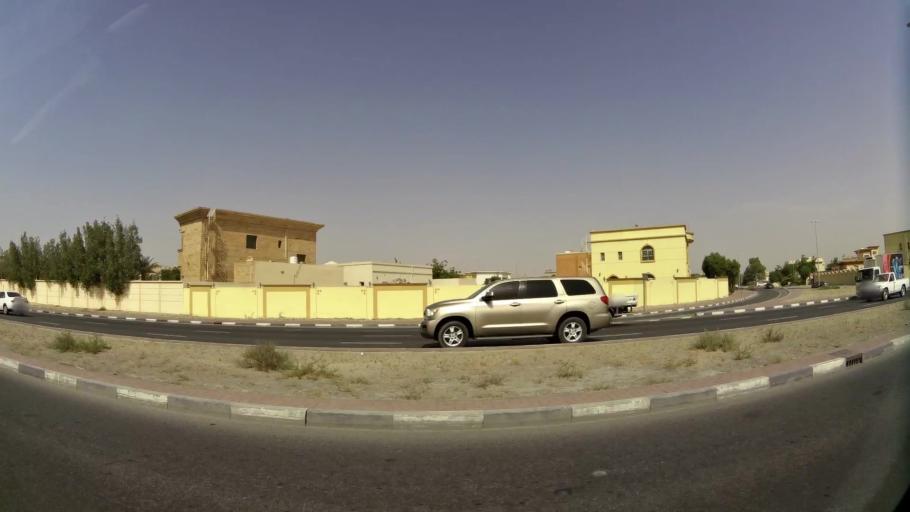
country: AE
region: Ash Shariqah
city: Sharjah
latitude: 25.2767
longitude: 55.3961
